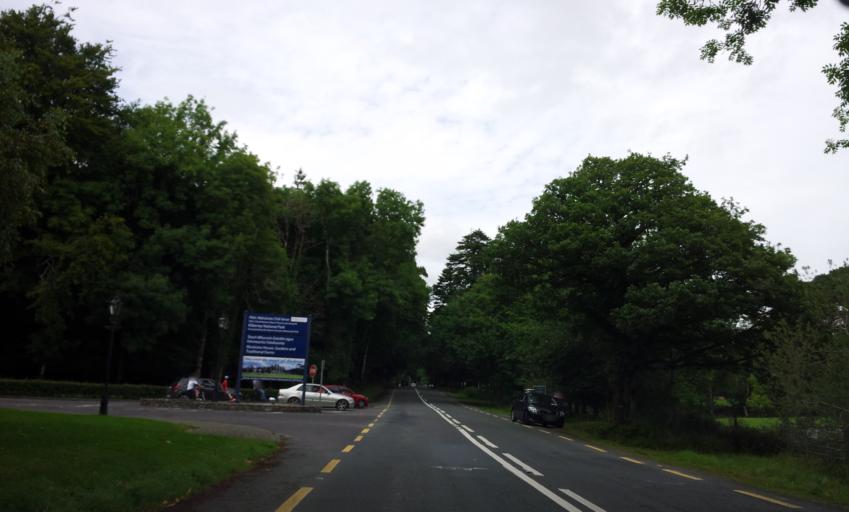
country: IE
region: Munster
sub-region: Ciarrai
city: Cill Airne
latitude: 52.0171
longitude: -9.4940
